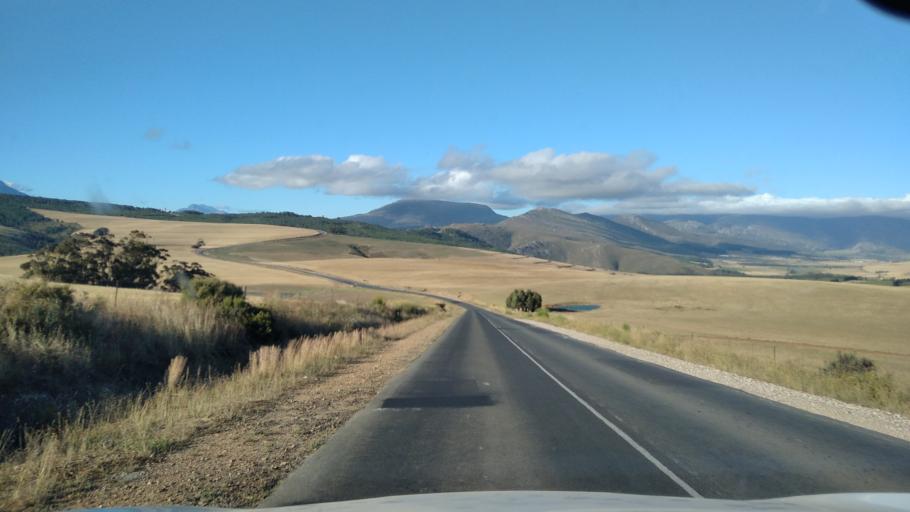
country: ZA
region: Western Cape
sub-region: Overberg District Municipality
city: Caledon
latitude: -34.1260
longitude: 19.2972
